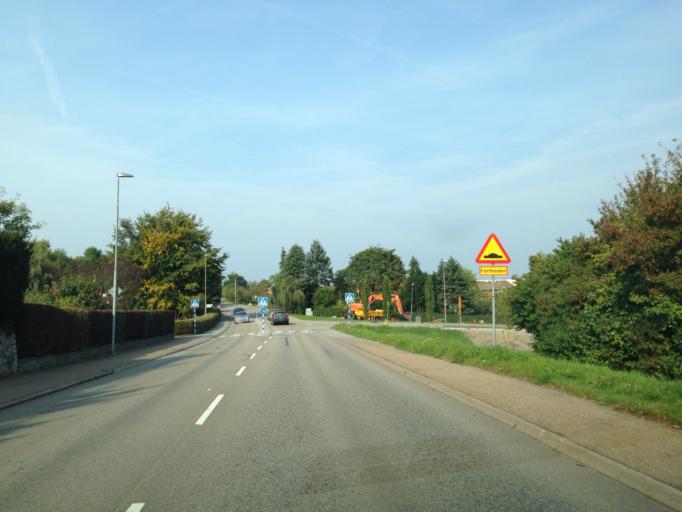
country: SE
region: Skane
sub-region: Bastads Kommun
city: Bastad
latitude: 56.4208
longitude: 12.8456
